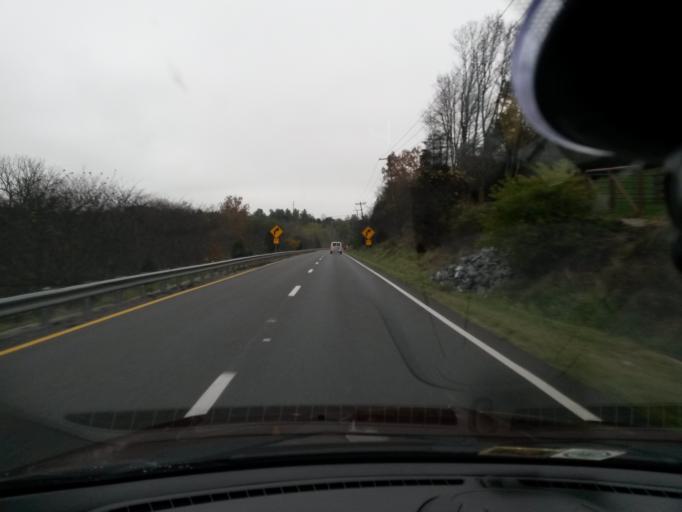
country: US
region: Virginia
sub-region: Botetourt County
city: Fincastle
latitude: 37.4652
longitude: -79.8822
